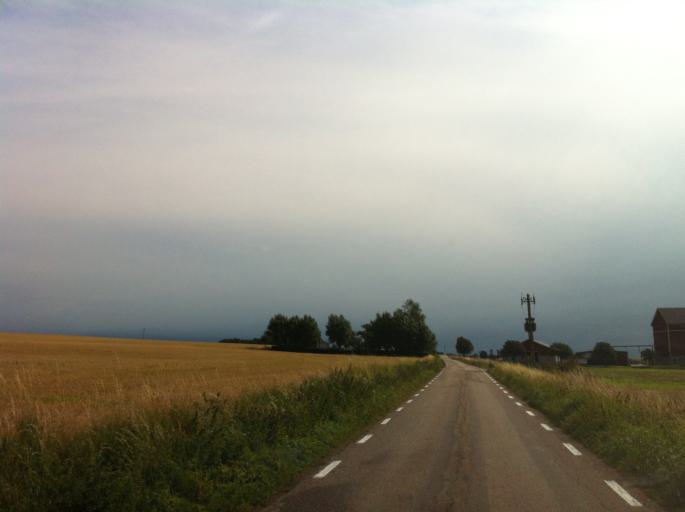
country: SE
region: Skane
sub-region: Landskrona
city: Landskrona
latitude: 55.9157
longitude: 12.8751
